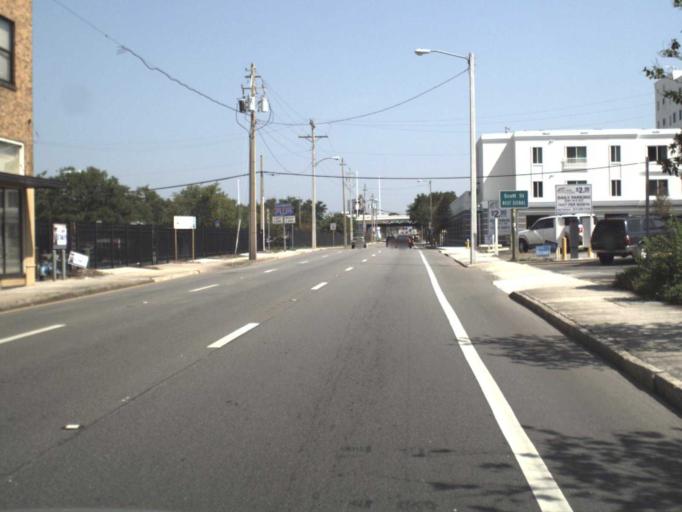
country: US
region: Florida
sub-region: Hillsborough County
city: Tampa
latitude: 27.9537
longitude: -82.4595
